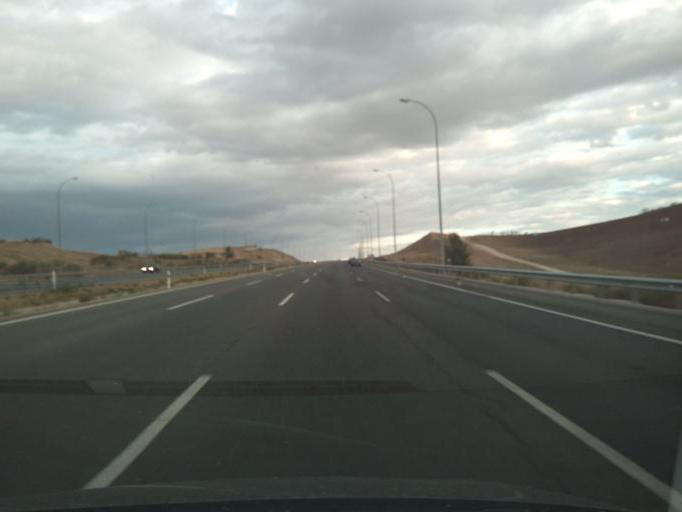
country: ES
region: Madrid
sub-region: Provincia de Madrid
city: Paracuellos de Jarama
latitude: 40.5368
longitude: -3.5272
